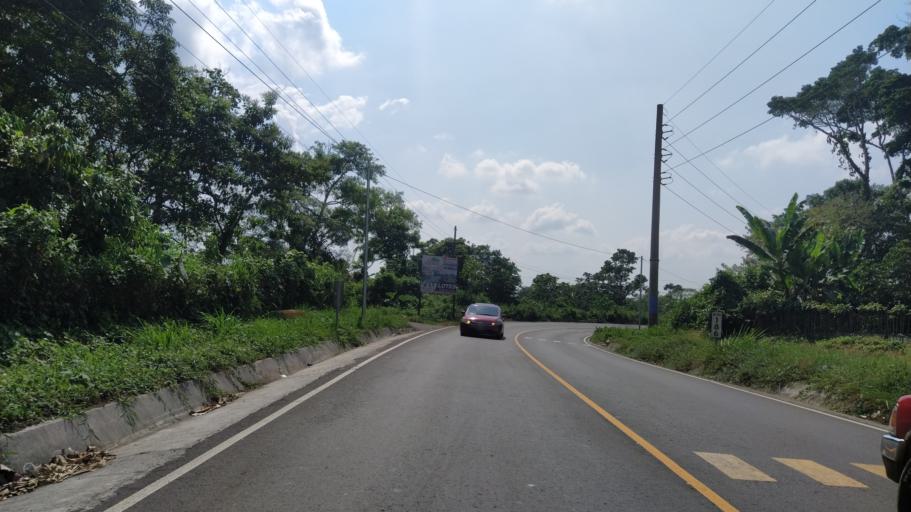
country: GT
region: Retalhuleu
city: San Felipe
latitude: 14.6210
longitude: -91.5861
